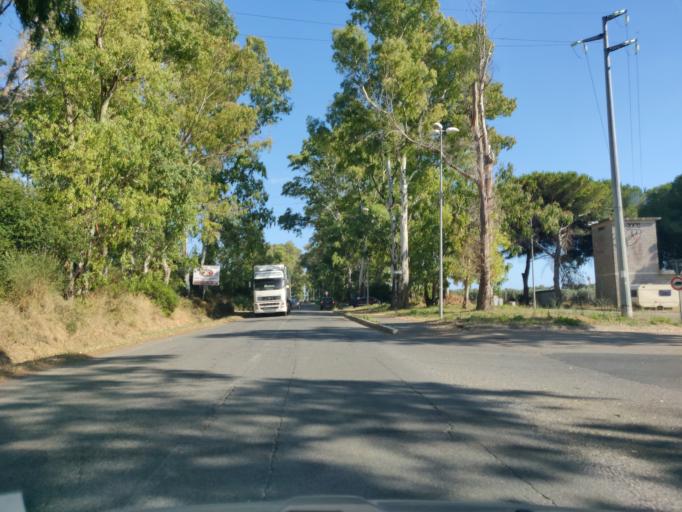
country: IT
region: Latium
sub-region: Citta metropolitana di Roma Capitale
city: Aurelia
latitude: 42.1457
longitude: 11.7624
